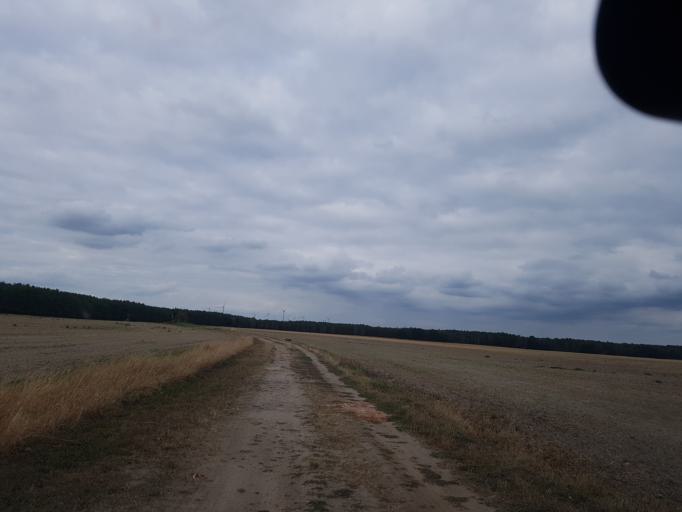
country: DE
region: Brandenburg
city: Schilda
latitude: 51.6373
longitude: 13.3299
